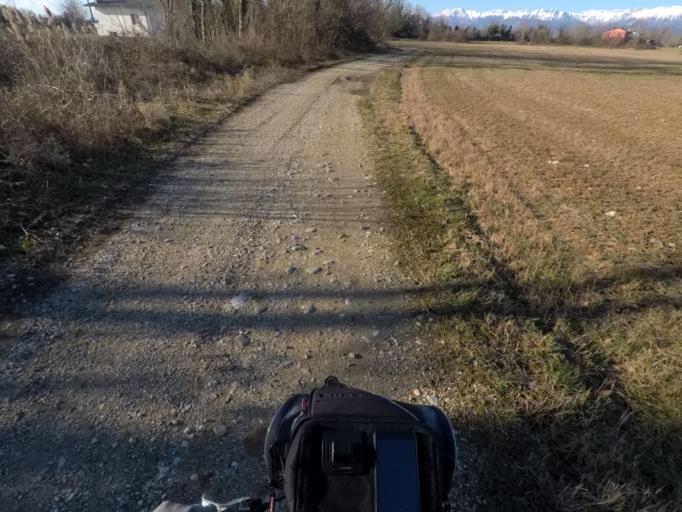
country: IT
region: Friuli Venezia Giulia
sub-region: Provincia di Udine
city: Remanzacco
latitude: 46.0998
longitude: 13.3248
